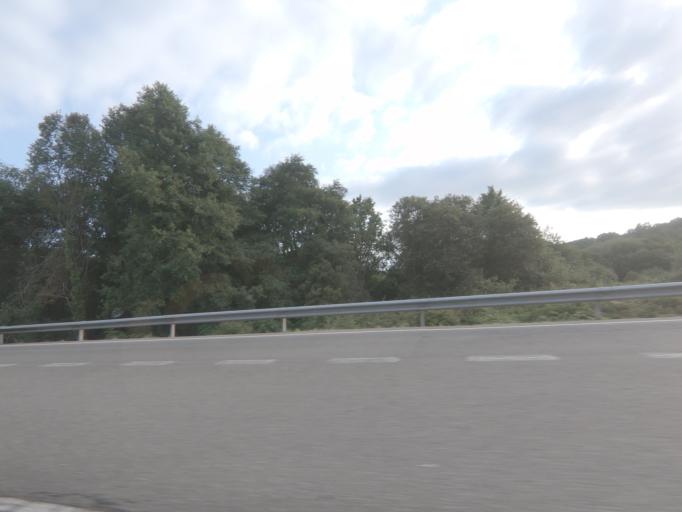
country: ES
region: Galicia
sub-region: Provincia de Ourense
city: Taboadela
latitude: 42.2212
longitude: -7.8422
